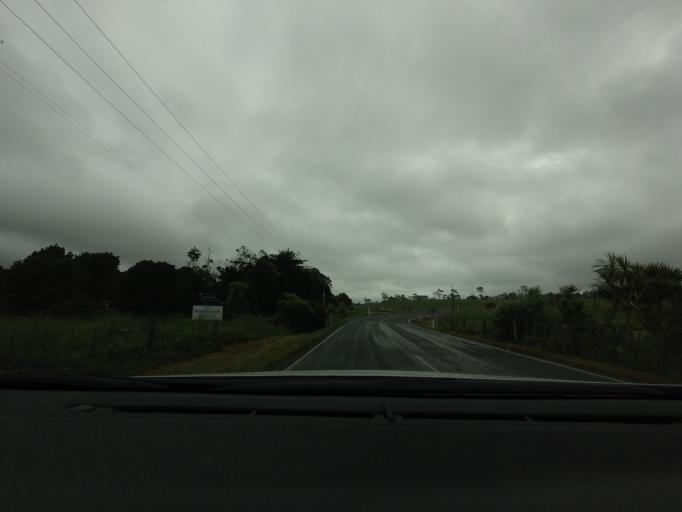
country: NZ
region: Auckland
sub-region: Auckland
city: Wellsford
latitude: -36.2836
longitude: 174.5665
